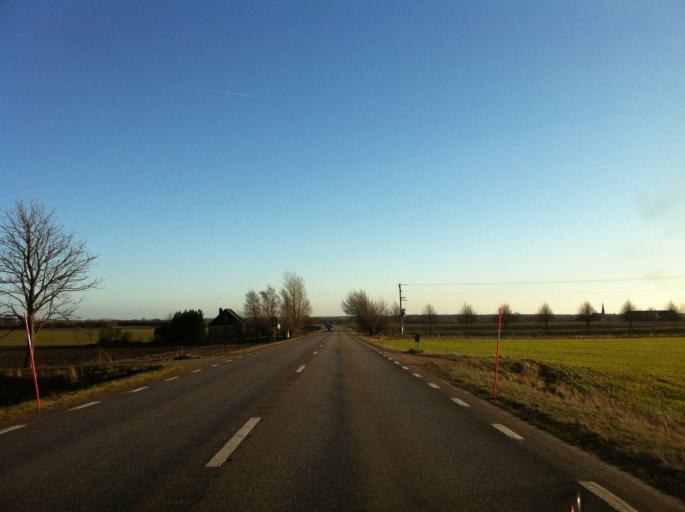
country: SE
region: Skane
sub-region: Landskrona
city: Asmundtorp
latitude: 55.9057
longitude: 12.9577
